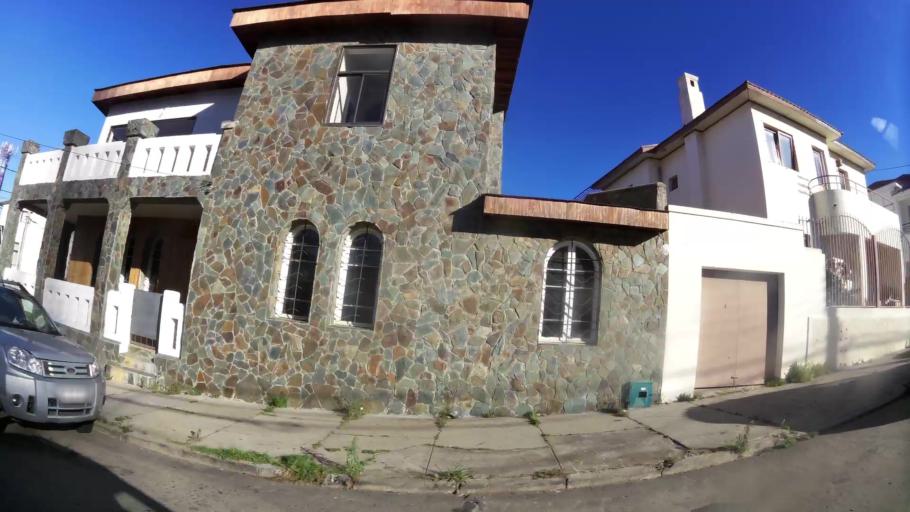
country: CL
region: Valparaiso
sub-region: Provincia de Valparaiso
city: Vina del Mar
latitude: -33.0319
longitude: -71.5797
